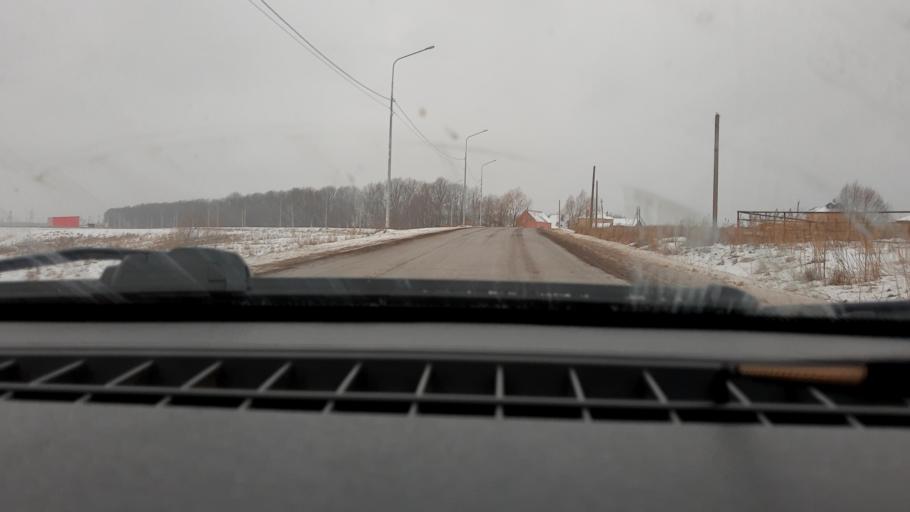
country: RU
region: Bashkortostan
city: Kabakovo
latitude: 54.7041
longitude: 56.2333
